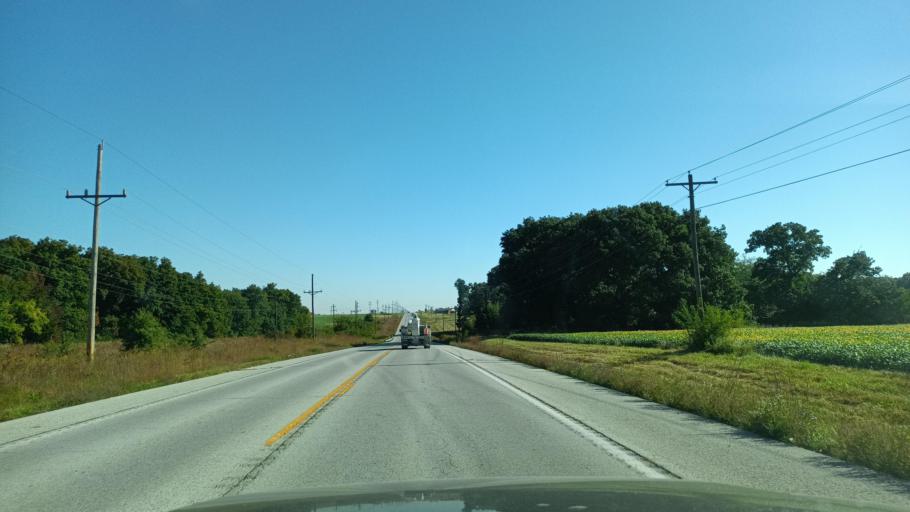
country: US
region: Missouri
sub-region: Audrain County
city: Vandalia
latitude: 39.4606
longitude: -91.6109
